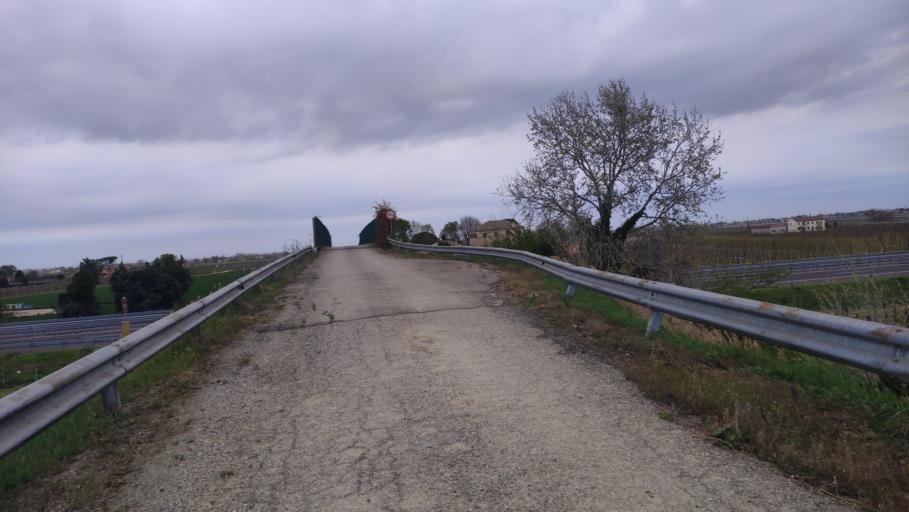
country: IT
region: Emilia-Romagna
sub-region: Provincia di Ravenna
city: Godo
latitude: 44.4004
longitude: 12.0537
